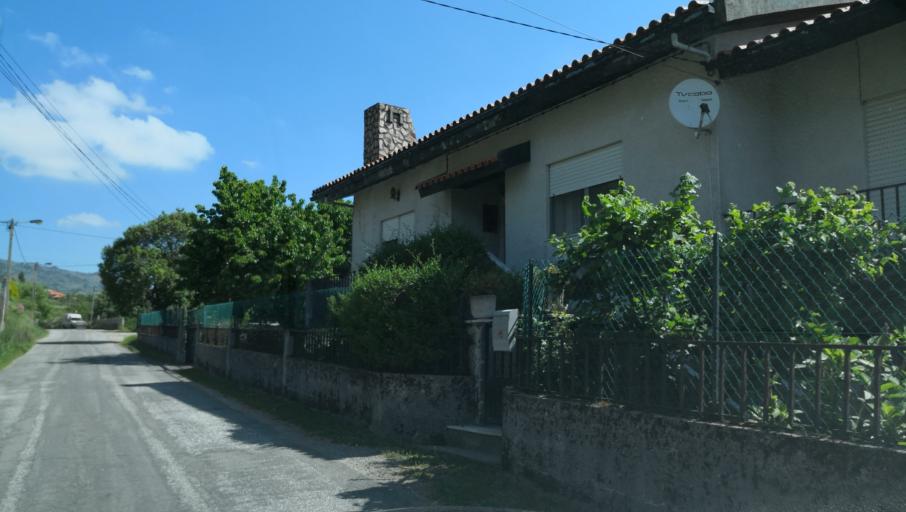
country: PT
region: Vila Real
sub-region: Vila Real
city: Vila Real
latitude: 41.3568
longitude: -7.7288
